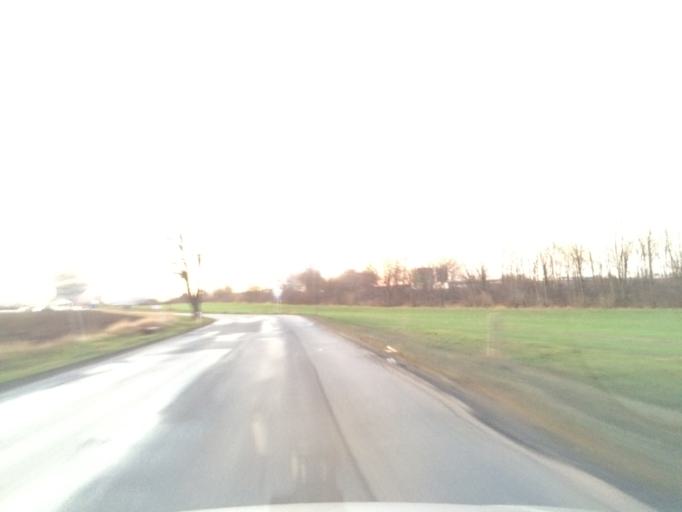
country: CZ
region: Central Bohemia
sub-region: Okres Kladno
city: Slany
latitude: 50.2254
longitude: 14.1140
